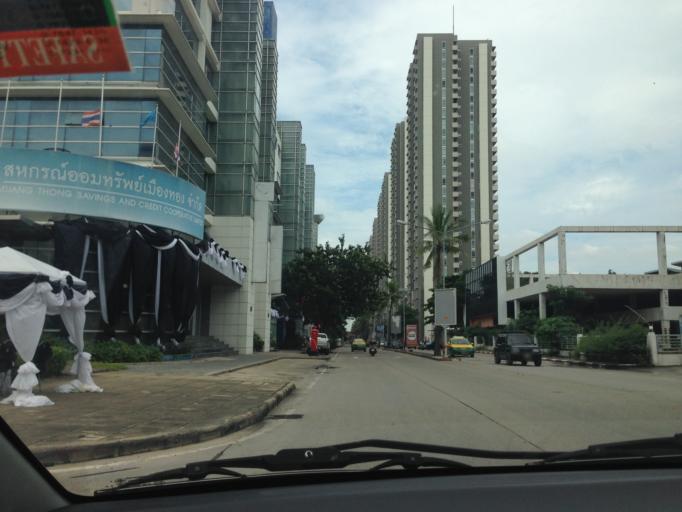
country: TH
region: Nonthaburi
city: Pak Kret
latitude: 13.9195
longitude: 100.5399
